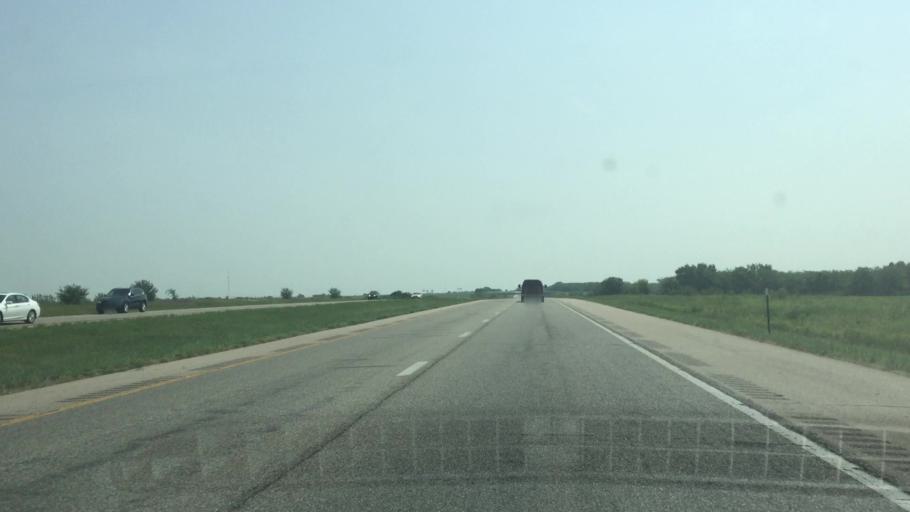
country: US
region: Kansas
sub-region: Osage County
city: Lyndon
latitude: 38.4264
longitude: -95.7629
